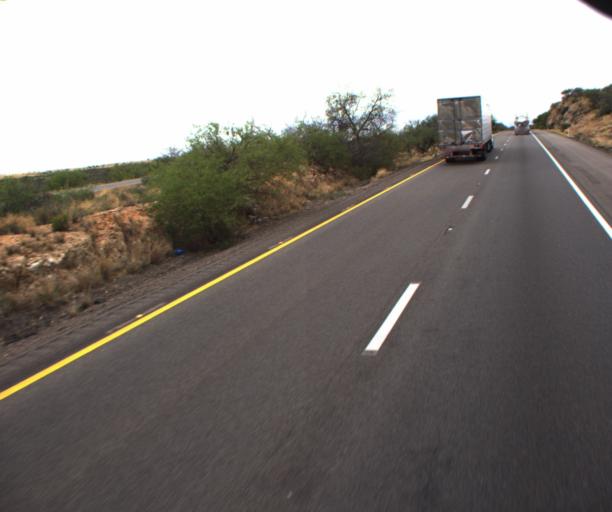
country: US
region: Arizona
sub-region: Cochise County
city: Saint David
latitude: 32.0097
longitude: -110.1303
